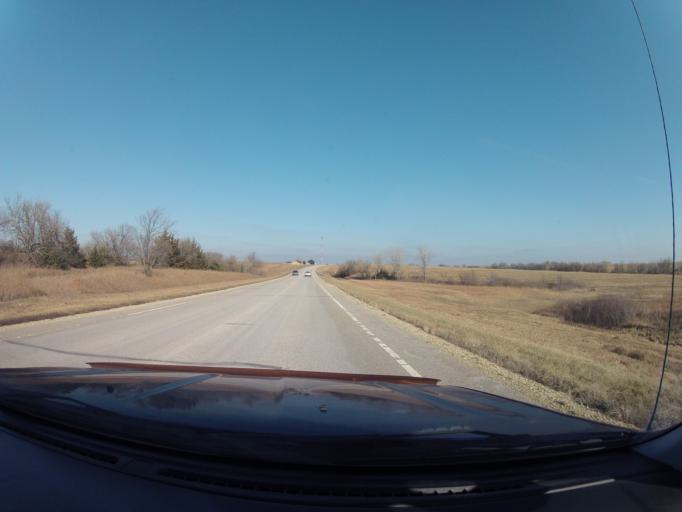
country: US
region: Kansas
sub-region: Marshall County
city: Blue Rapids
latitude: 39.5572
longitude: -96.7553
